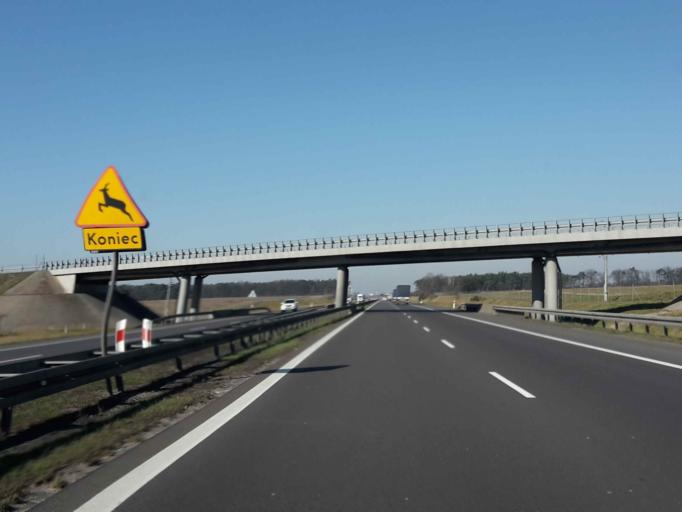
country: PL
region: Greater Poland Voivodeship
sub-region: Powiat poznanski
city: Swarzedz
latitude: 52.3349
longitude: 17.0644
